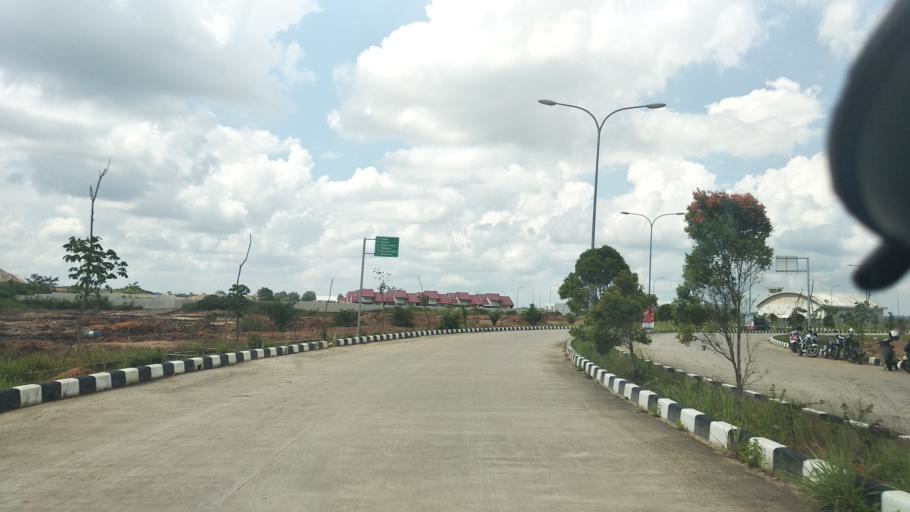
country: ID
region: East Kalimantan
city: Samarinda
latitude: -0.3729
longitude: 117.2603
